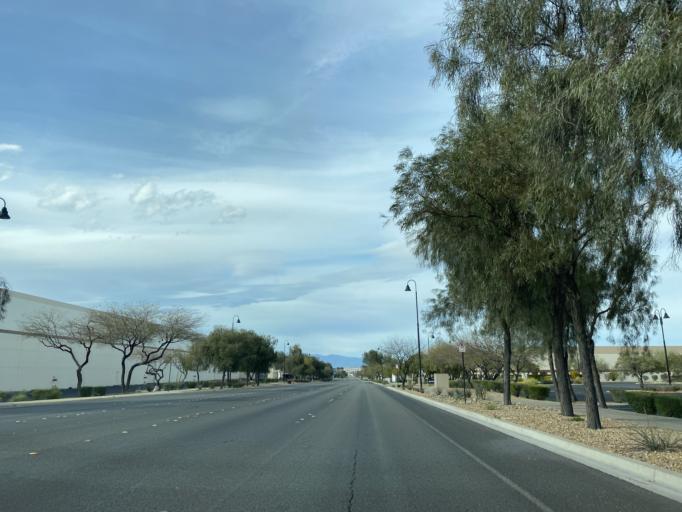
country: US
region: Nevada
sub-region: Clark County
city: Henderson
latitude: 36.0508
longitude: -115.0197
